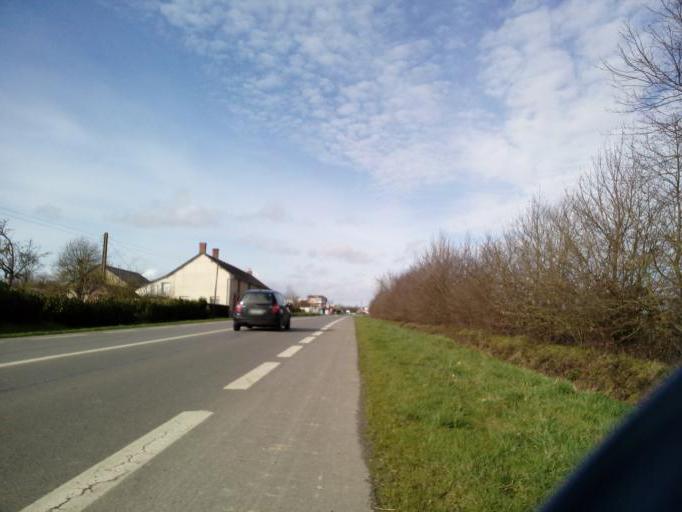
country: FR
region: Brittany
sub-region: Departement d'Ille-et-Vilaine
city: Montgermont
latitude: 48.1693
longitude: -1.7184
